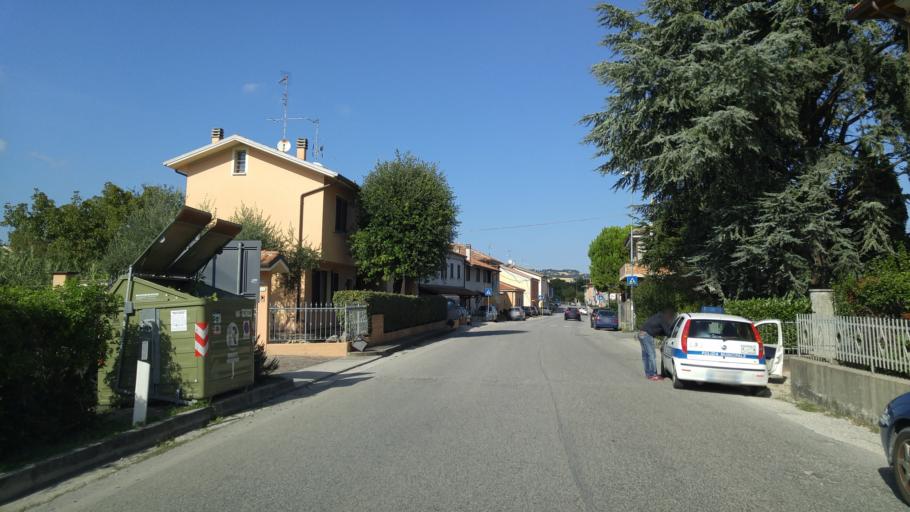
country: IT
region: The Marches
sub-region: Provincia di Pesaro e Urbino
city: Lucrezia
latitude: 43.7794
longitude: 12.9416
